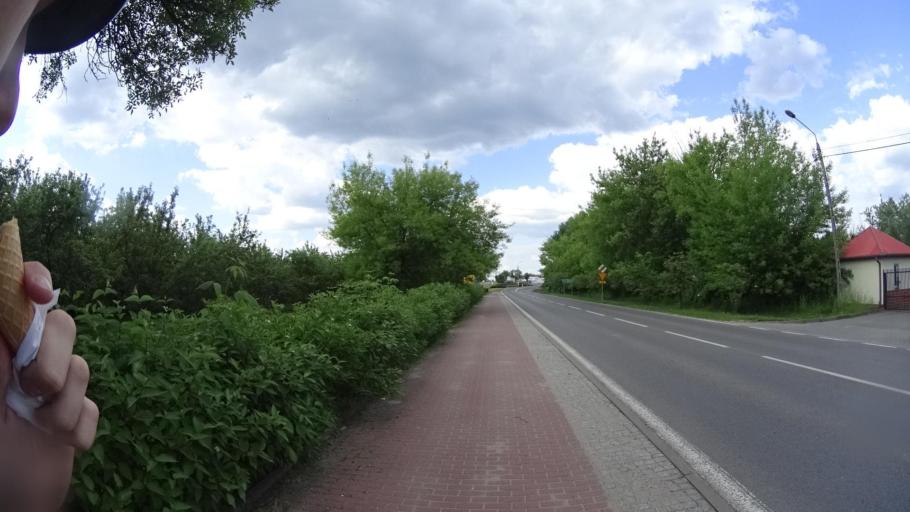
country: PL
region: Masovian Voivodeship
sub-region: Powiat piaseczynski
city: Tarczyn
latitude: 51.9936
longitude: 20.8400
